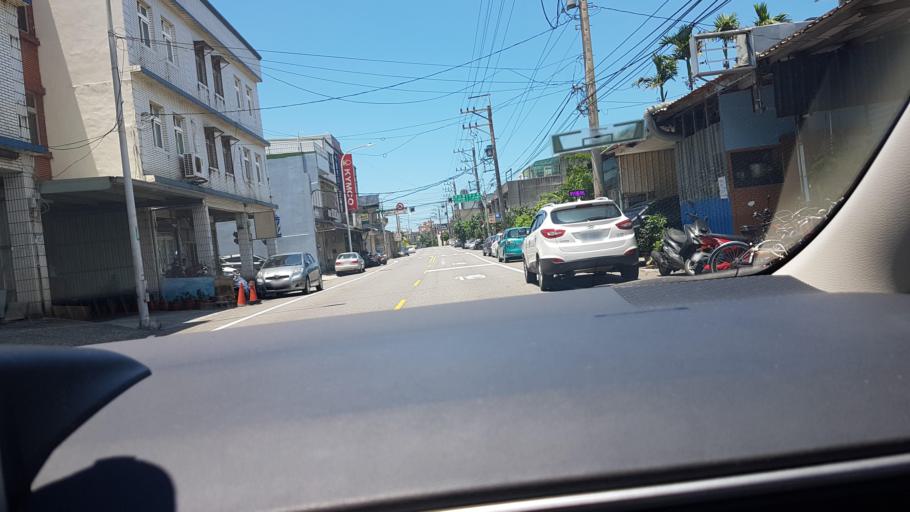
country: TW
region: Taiwan
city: Taoyuan City
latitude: 25.1017
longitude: 121.2605
